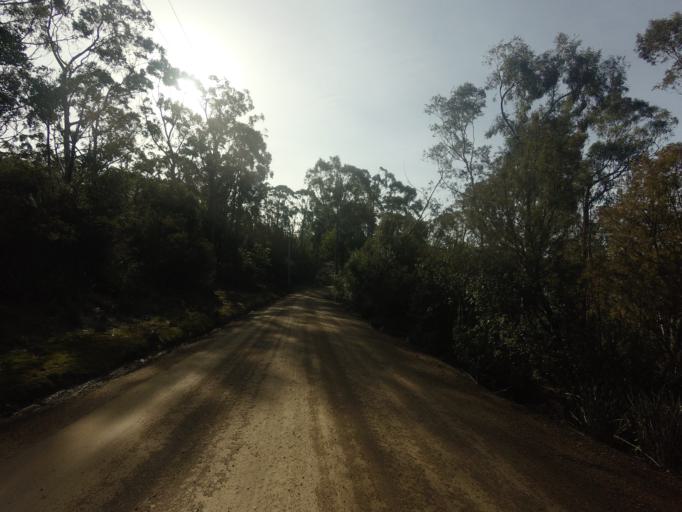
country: AU
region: Tasmania
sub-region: Kingborough
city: Kettering
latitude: -43.1166
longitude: 147.2706
